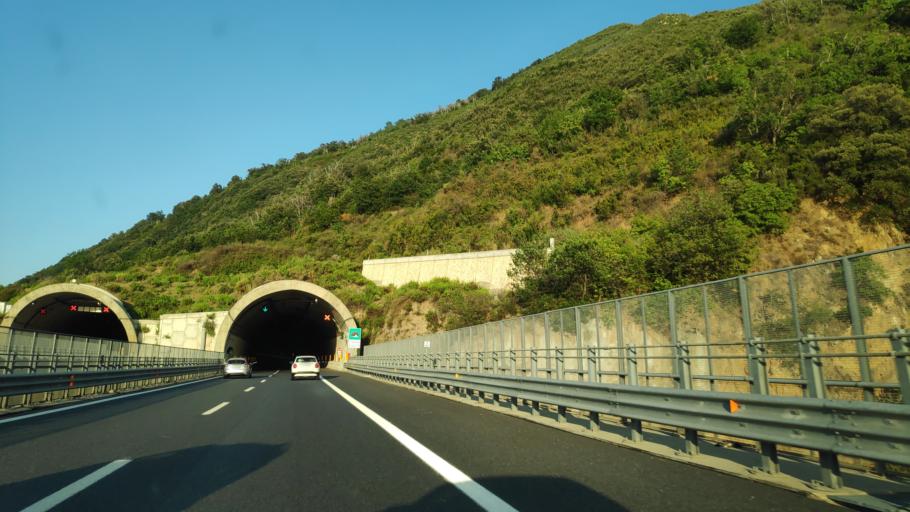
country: IT
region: Calabria
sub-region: Provincia di Reggio Calabria
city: Scilla
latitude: 38.2486
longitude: 15.7317
